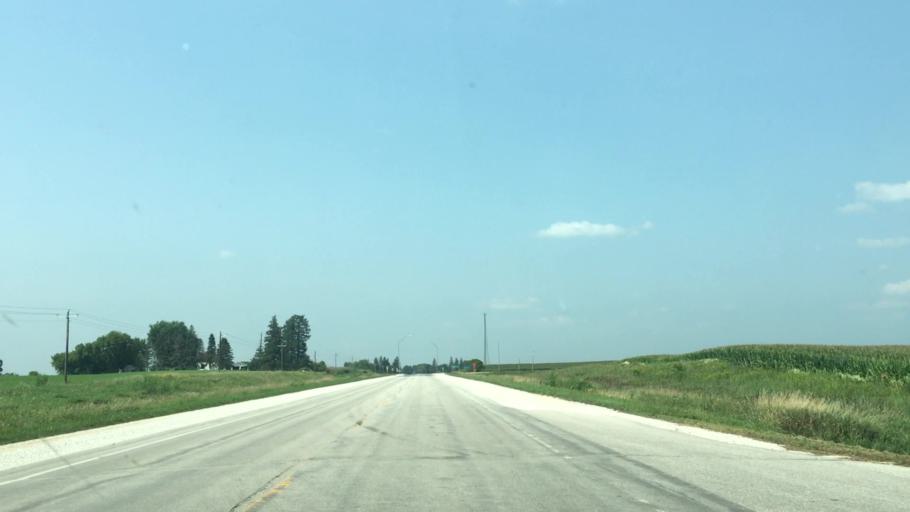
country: US
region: Iowa
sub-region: Winneshiek County
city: Decorah
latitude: 43.4395
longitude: -91.8614
